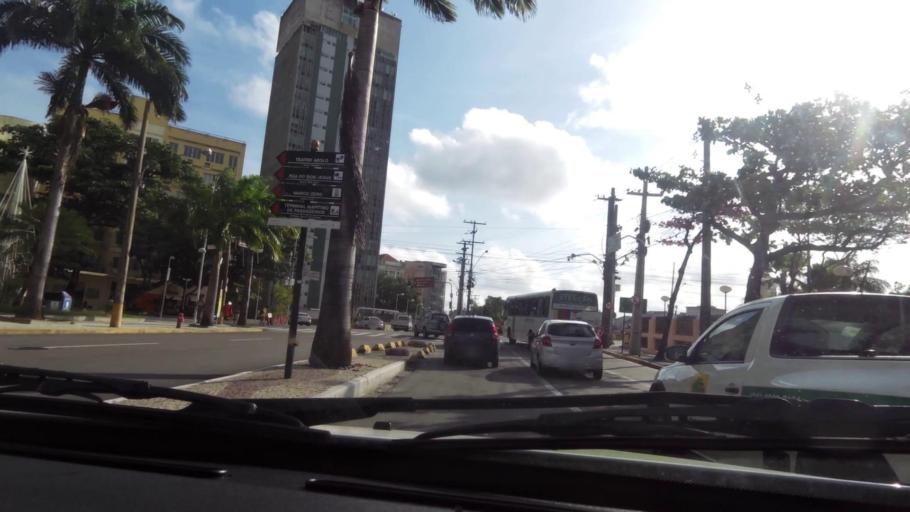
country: BR
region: Pernambuco
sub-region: Recife
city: Recife
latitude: -8.0620
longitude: -34.8737
